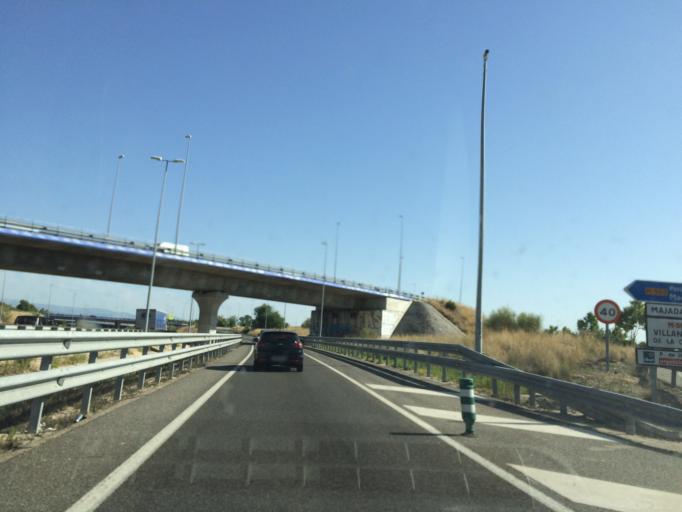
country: ES
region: Madrid
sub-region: Provincia de Madrid
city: Majadahonda
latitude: 40.4505
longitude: -3.8788
